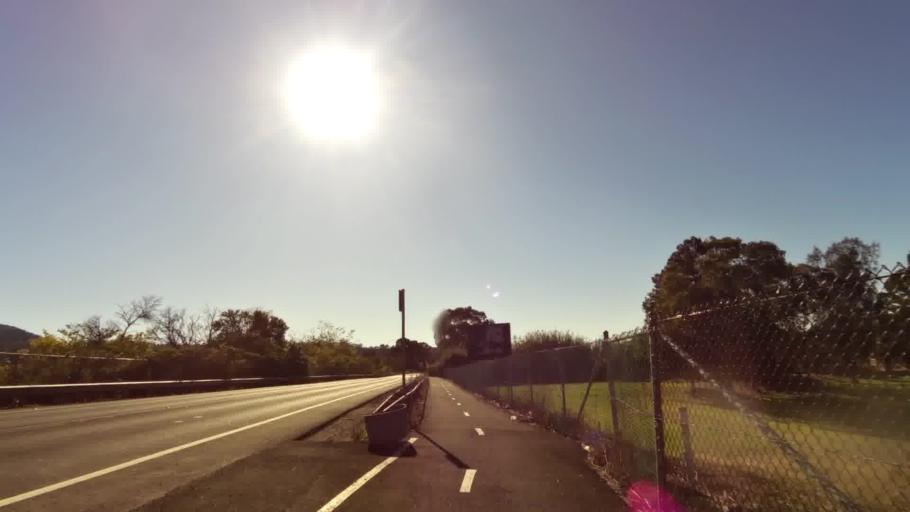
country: AU
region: New South Wales
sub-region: Wollongong
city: Koonawarra
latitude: -34.4769
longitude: 150.8082
